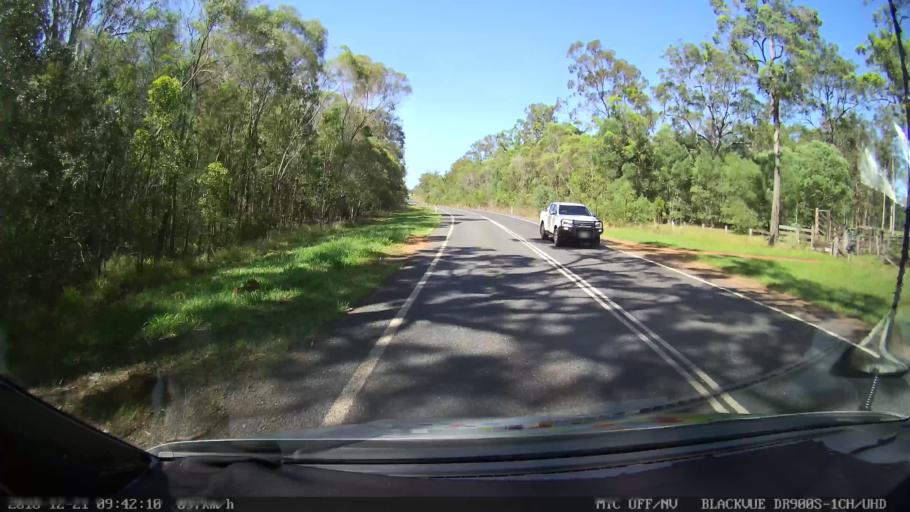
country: AU
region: New South Wales
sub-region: Clarence Valley
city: Grafton
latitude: -29.5931
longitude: 152.9493
